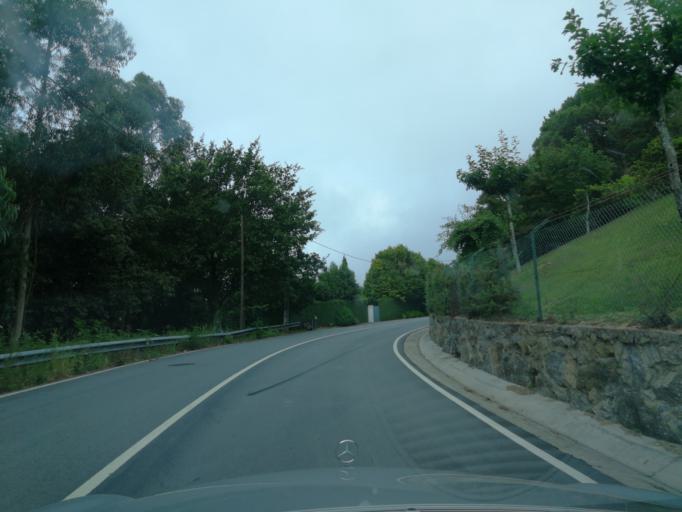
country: PT
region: Braga
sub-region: Braga
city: Braga
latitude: 41.5168
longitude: -8.3717
